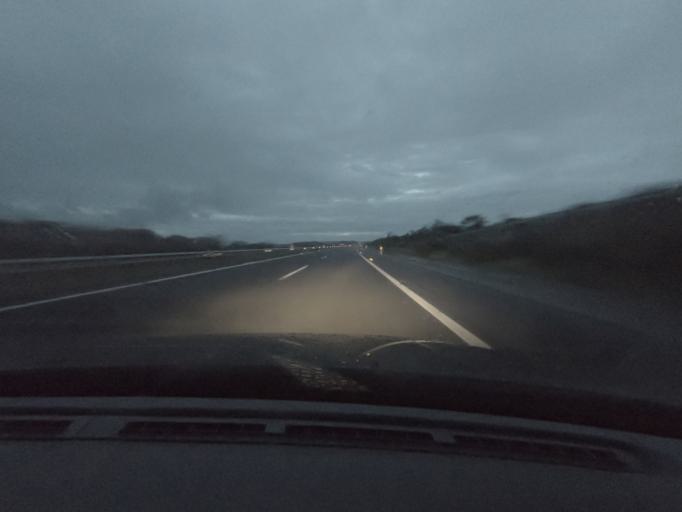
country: ES
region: Extremadura
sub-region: Provincia de Caceres
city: Caceres
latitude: 39.3939
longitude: -6.3750
